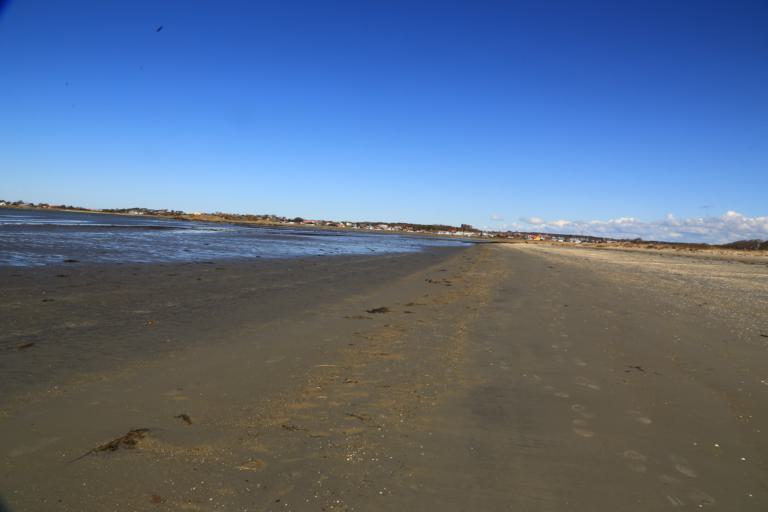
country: SE
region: Halland
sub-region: Varbergs Kommun
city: Traslovslage
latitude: 57.0632
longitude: 12.2769
